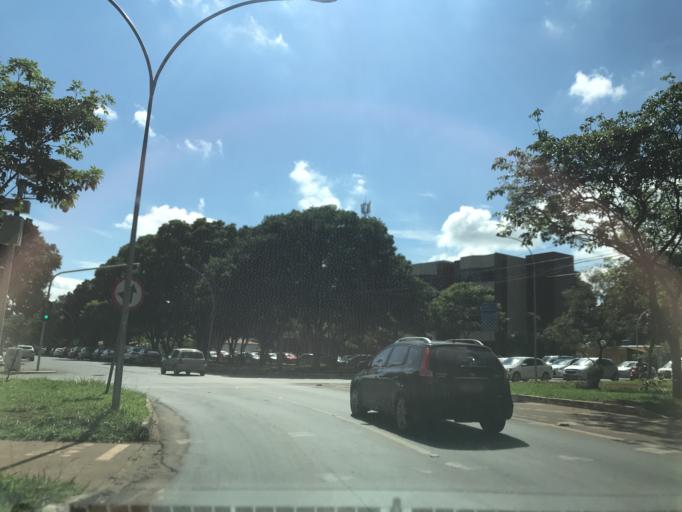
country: BR
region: Federal District
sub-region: Brasilia
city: Brasilia
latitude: -15.7702
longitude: -47.8925
